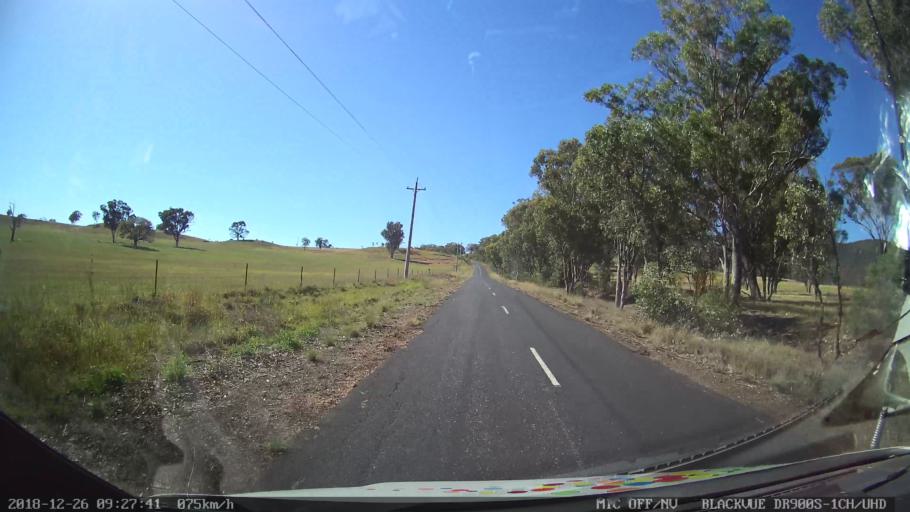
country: AU
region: New South Wales
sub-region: Mid-Western Regional
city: Kandos
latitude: -32.8384
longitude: 150.0182
